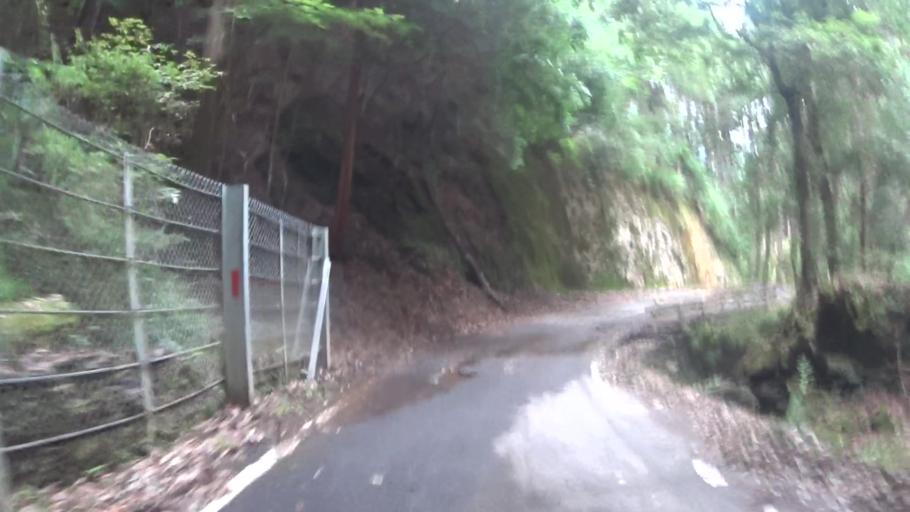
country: JP
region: Kyoto
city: Kameoka
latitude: 35.1572
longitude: 135.5730
